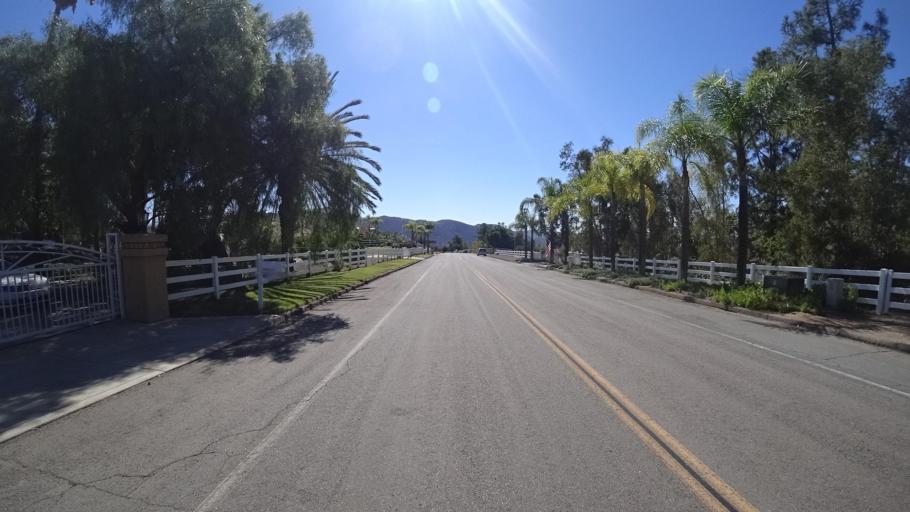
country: US
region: California
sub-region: San Diego County
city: Harbison Canyon
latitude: 32.8735
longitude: -116.8376
